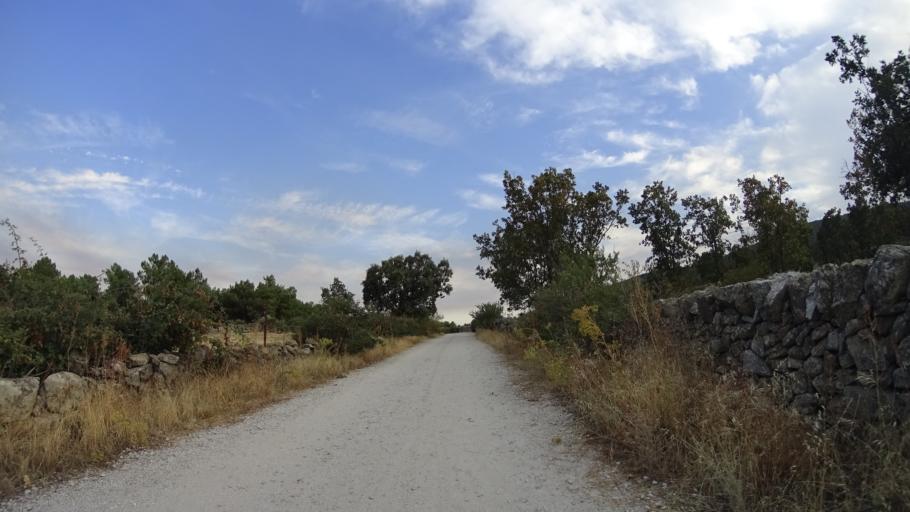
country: ES
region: Madrid
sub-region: Provincia de Madrid
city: Moralzarzal
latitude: 40.6956
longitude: -3.9740
